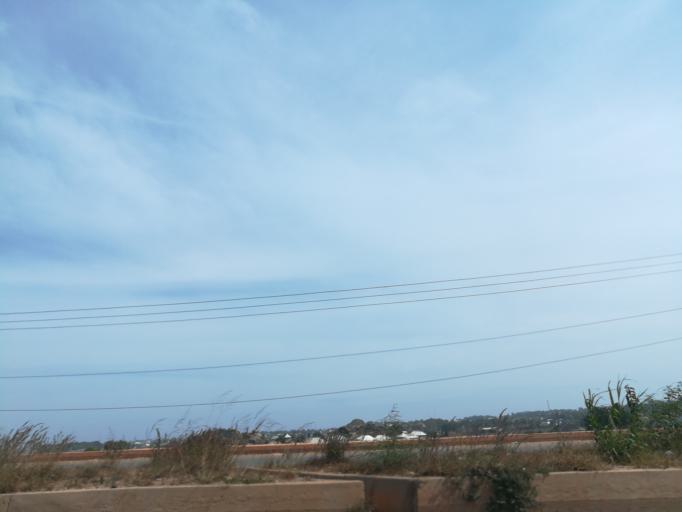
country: NG
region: Plateau
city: Bukuru
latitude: 9.8263
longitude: 8.8663
